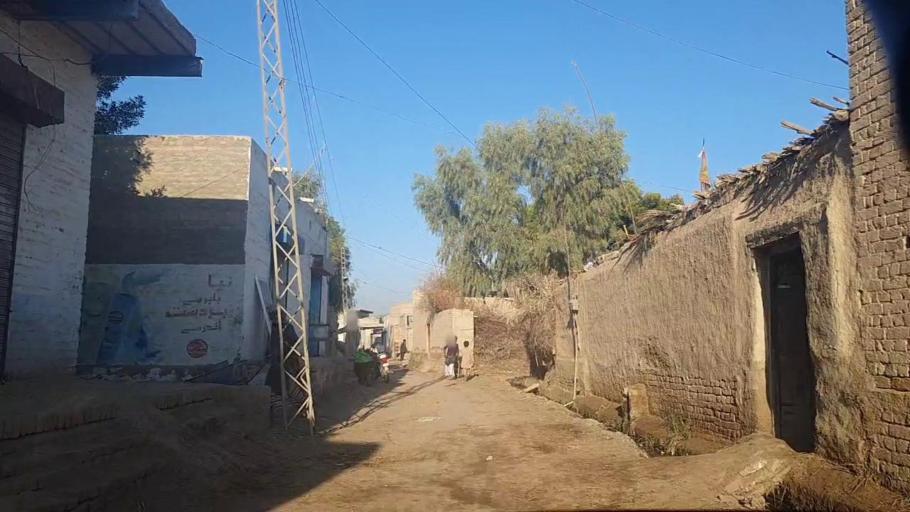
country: PK
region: Sindh
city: Sobhadero
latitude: 27.3978
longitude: 68.4207
